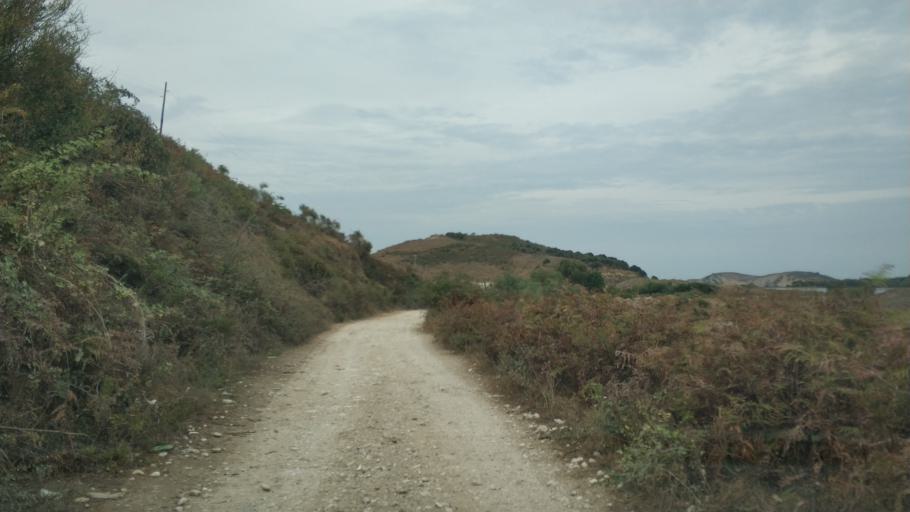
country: AL
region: Vlore
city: Vlore
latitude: 40.5135
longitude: 19.3975
